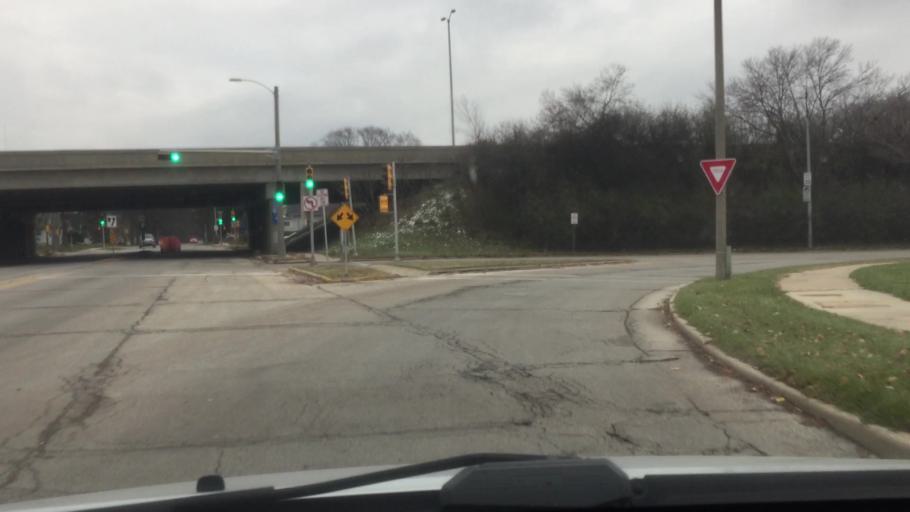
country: US
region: Wisconsin
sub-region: Milwaukee County
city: West Allis
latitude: 43.0309
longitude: -87.9975
